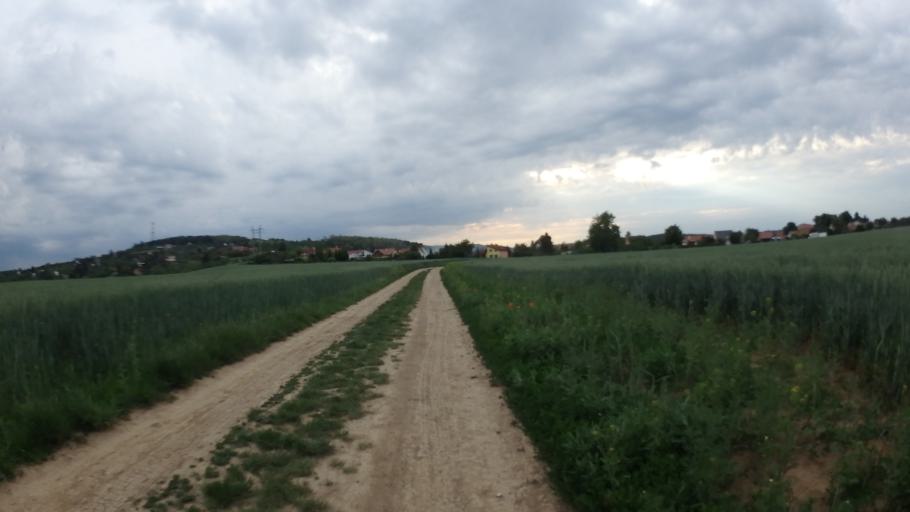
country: CZ
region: South Moravian
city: Moravany
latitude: 49.1392
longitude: 16.5582
